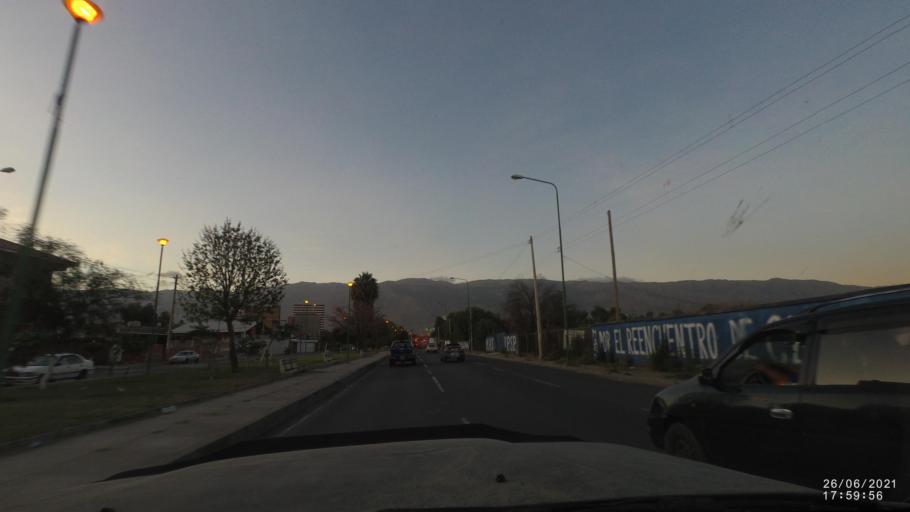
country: BO
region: Cochabamba
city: Cochabamba
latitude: -17.3892
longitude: -66.1825
